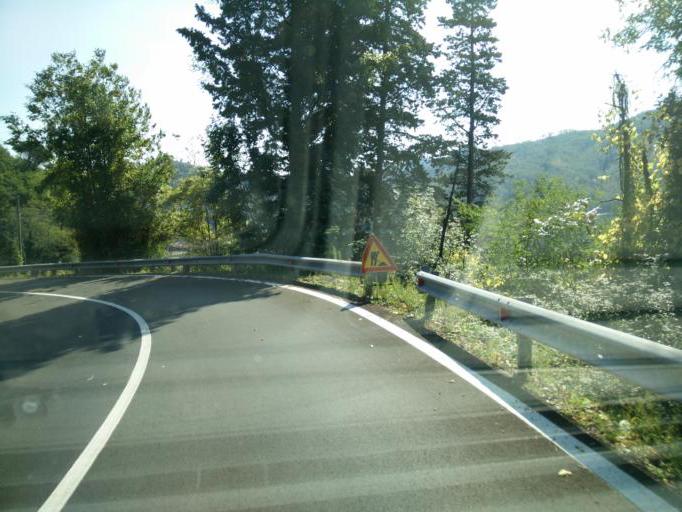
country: IT
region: Liguria
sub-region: Provincia di La Spezia
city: Carrodano
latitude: 44.2452
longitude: 9.6507
